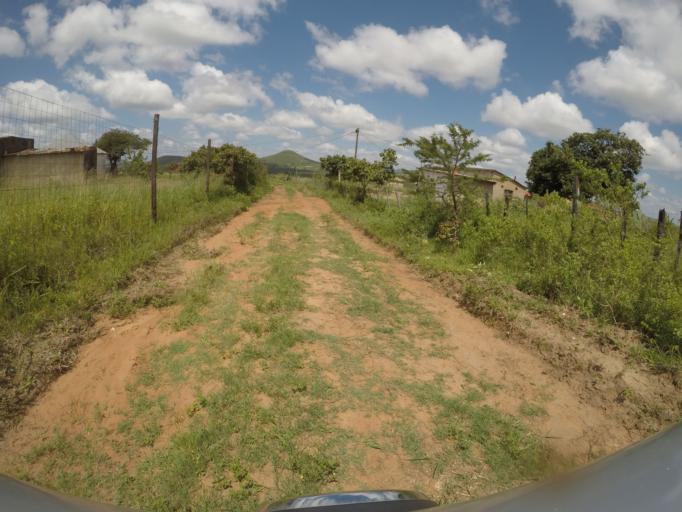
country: ZA
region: KwaZulu-Natal
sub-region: uThungulu District Municipality
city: Empangeni
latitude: -28.5816
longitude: 31.8434
